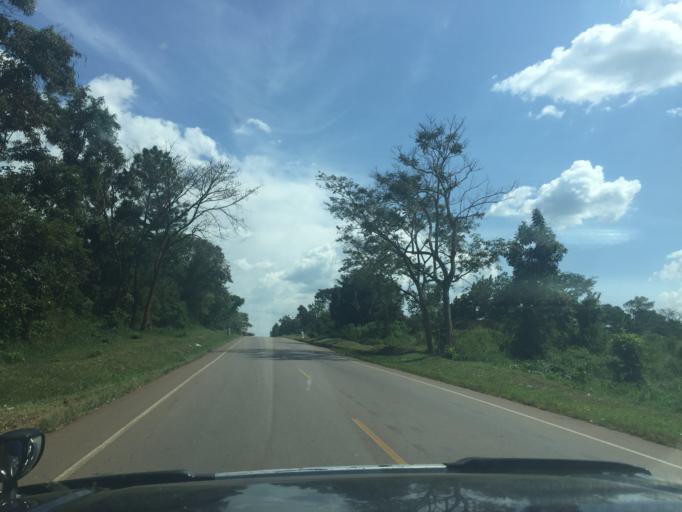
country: UG
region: Central Region
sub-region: Luwero District
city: Luwero
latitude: 0.8037
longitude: 32.5065
